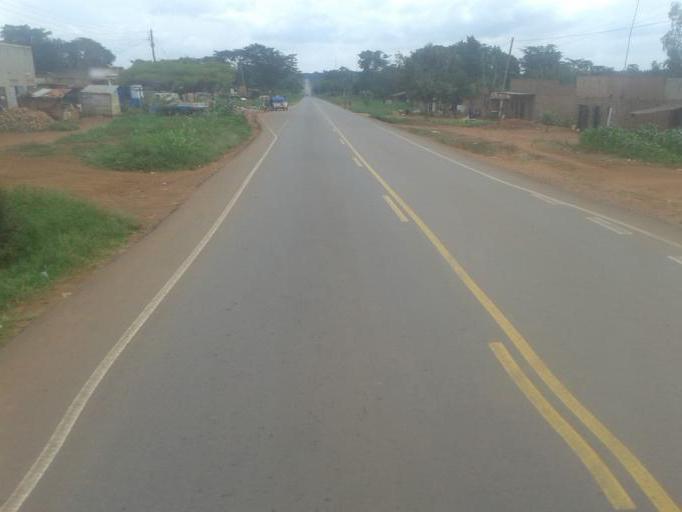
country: UG
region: Central Region
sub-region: Luwero District
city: Luwero
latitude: 0.8987
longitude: 32.4776
